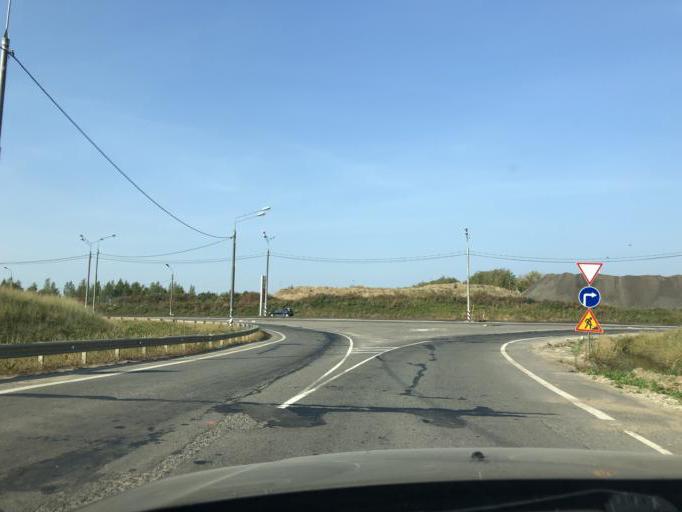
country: RU
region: Tula
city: Novogurovskiy
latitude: 54.4690
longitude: 37.5127
